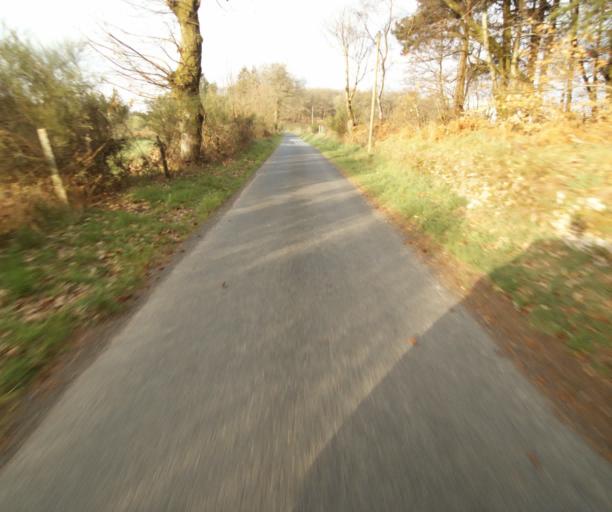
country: FR
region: Limousin
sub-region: Departement de la Correze
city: Correze
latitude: 45.3996
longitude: 1.8682
